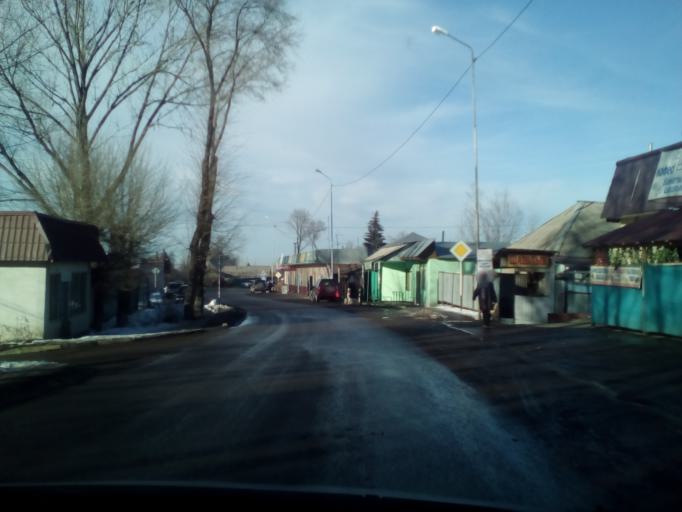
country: KZ
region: Almaty Oblysy
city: Burunday
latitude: 43.1612
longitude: 76.4165
